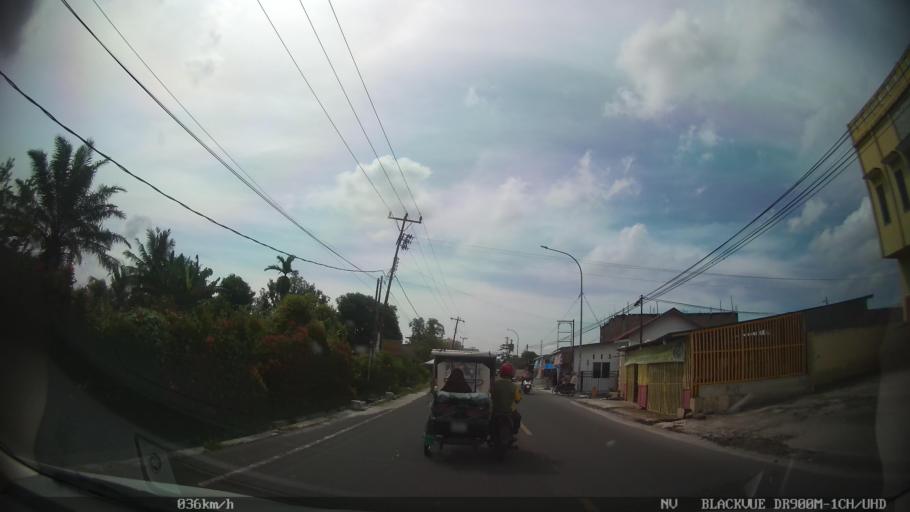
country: ID
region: North Sumatra
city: Percut
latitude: 3.5775
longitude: 98.8659
